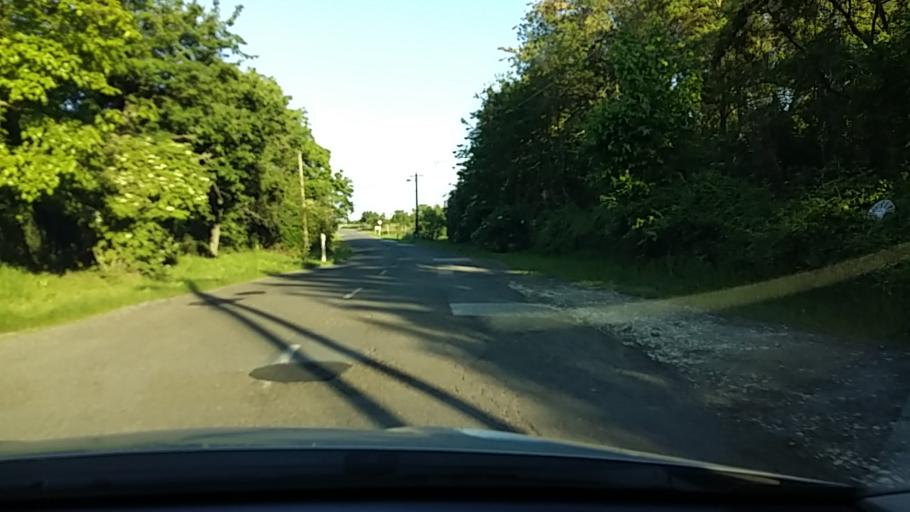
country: HU
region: Nograd
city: Diosjeno
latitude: 47.9083
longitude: 19.0556
